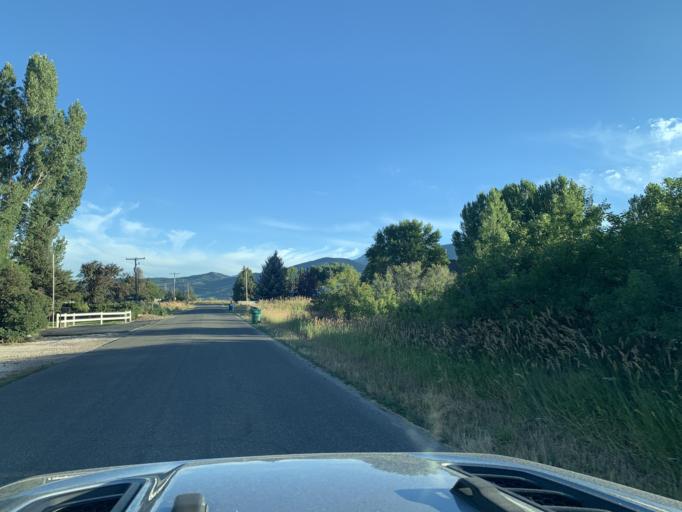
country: US
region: Utah
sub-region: Weber County
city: Wolf Creek
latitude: 41.2956
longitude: -111.8104
